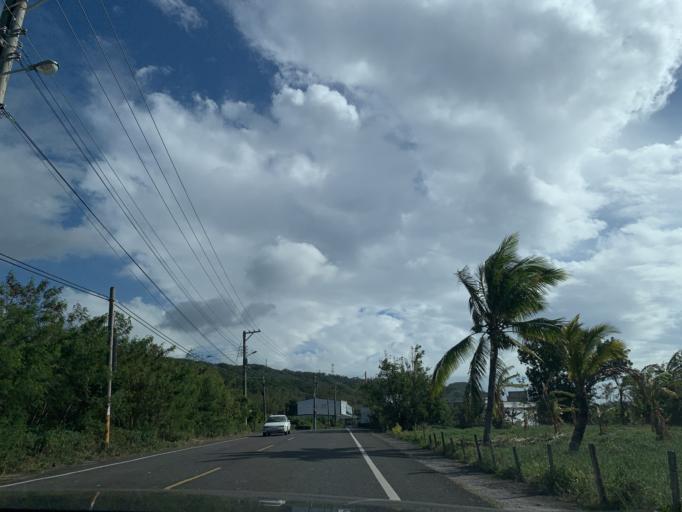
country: TW
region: Taiwan
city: Hengchun
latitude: 22.0014
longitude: 120.7535
